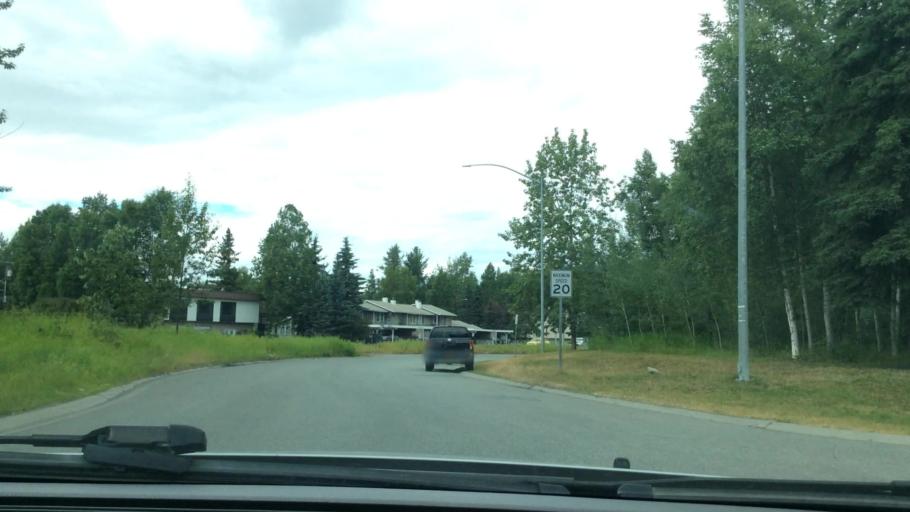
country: US
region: Alaska
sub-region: Anchorage Municipality
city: Anchorage
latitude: 61.1992
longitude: -149.7773
